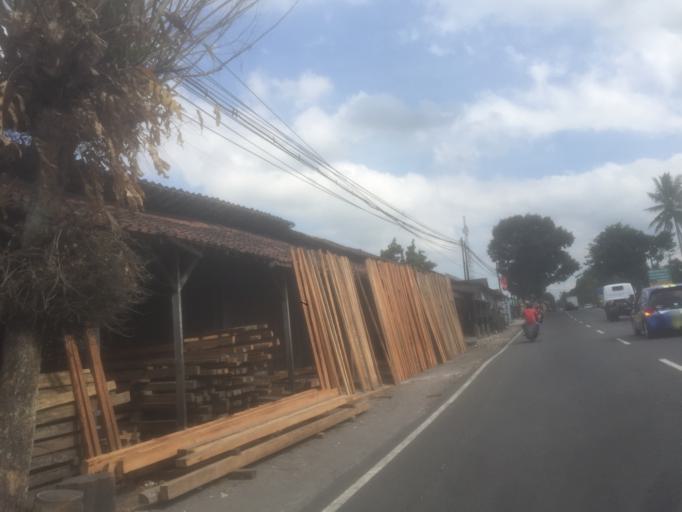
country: ID
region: Daerah Istimewa Yogyakarta
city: Sleman
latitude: -7.6675
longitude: 110.3323
